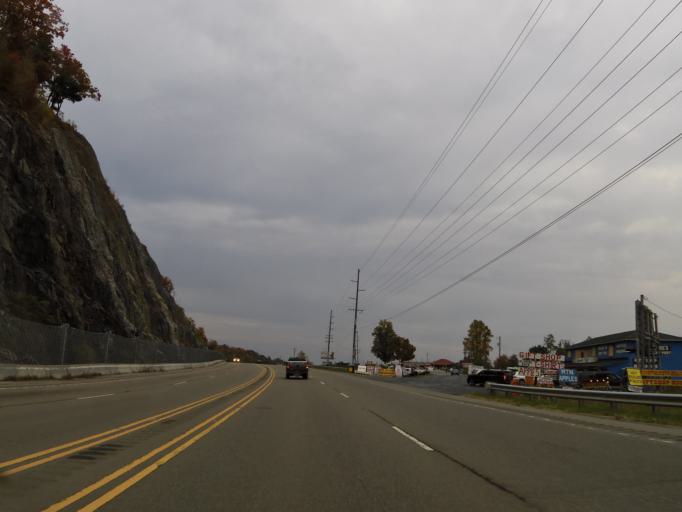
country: US
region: North Carolina
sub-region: Watauga County
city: Blowing Rock
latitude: 36.0973
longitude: -81.6413
